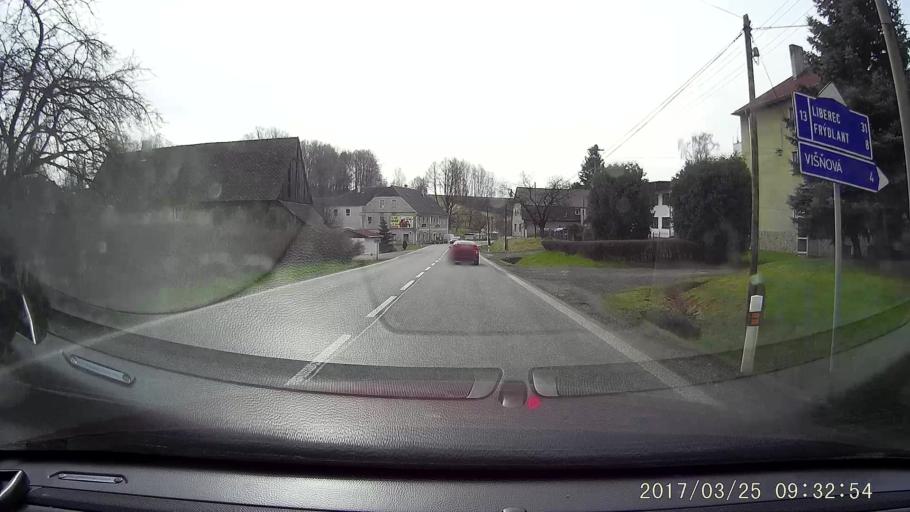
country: PL
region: Silesian Voivodeship
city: Zawidow
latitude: 50.9814
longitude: 15.0766
